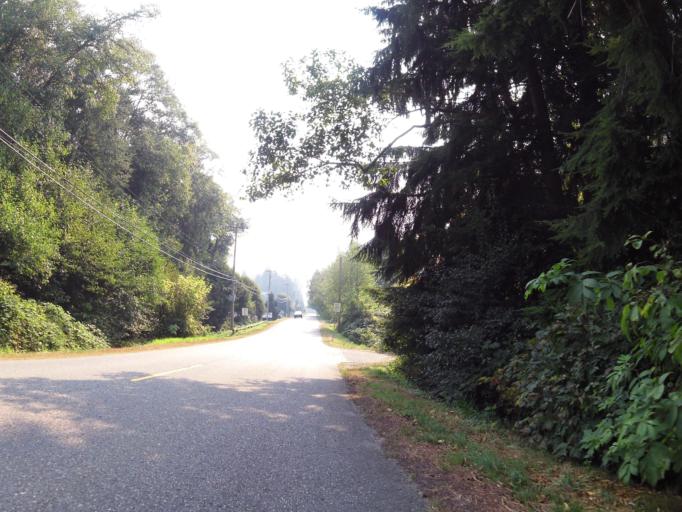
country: US
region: Washington
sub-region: Whatcom County
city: Blaine
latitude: 49.0231
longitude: -122.7573
